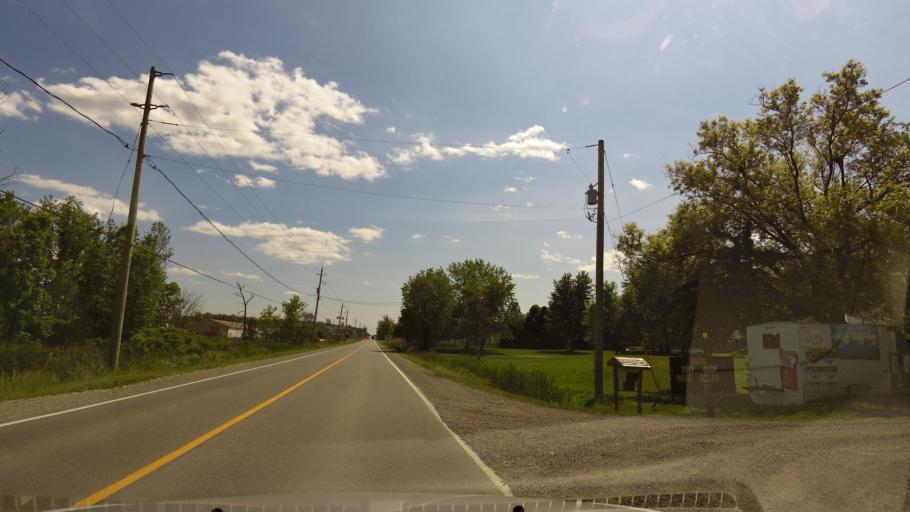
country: CA
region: Ontario
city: Brantford
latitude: 43.0932
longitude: -80.1021
